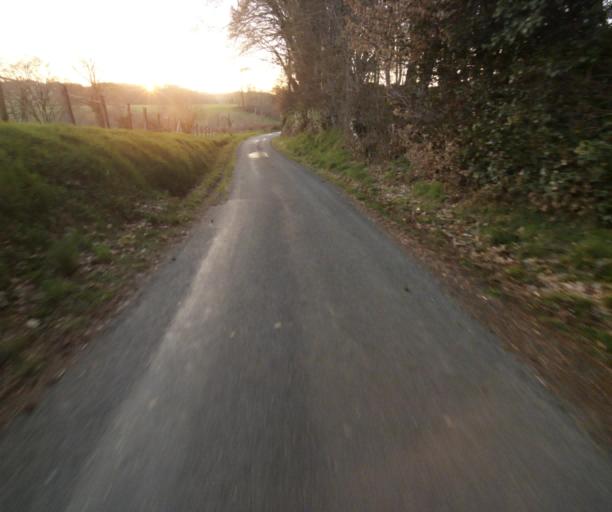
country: FR
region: Limousin
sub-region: Departement de la Correze
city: Saint-Clement
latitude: 45.3660
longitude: 1.6195
